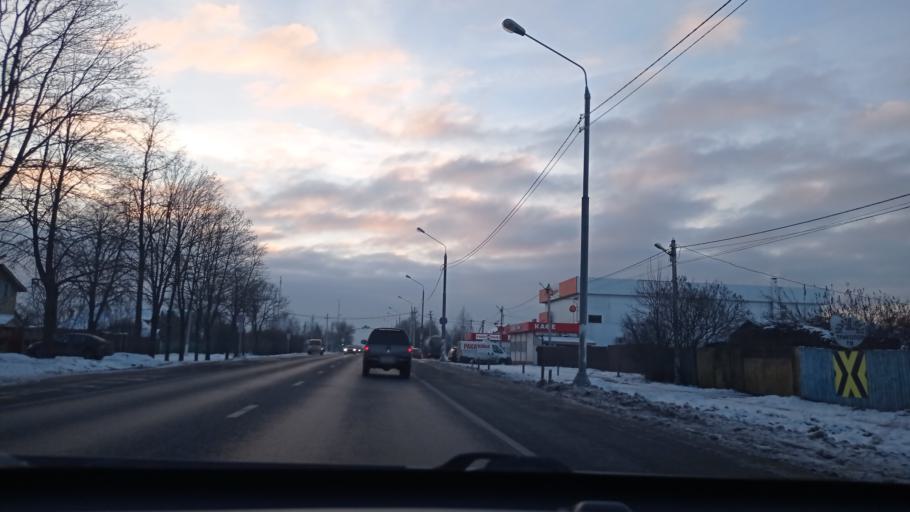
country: RU
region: Moskovskaya
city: Selyatino
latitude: 55.2629
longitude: 37.1056
